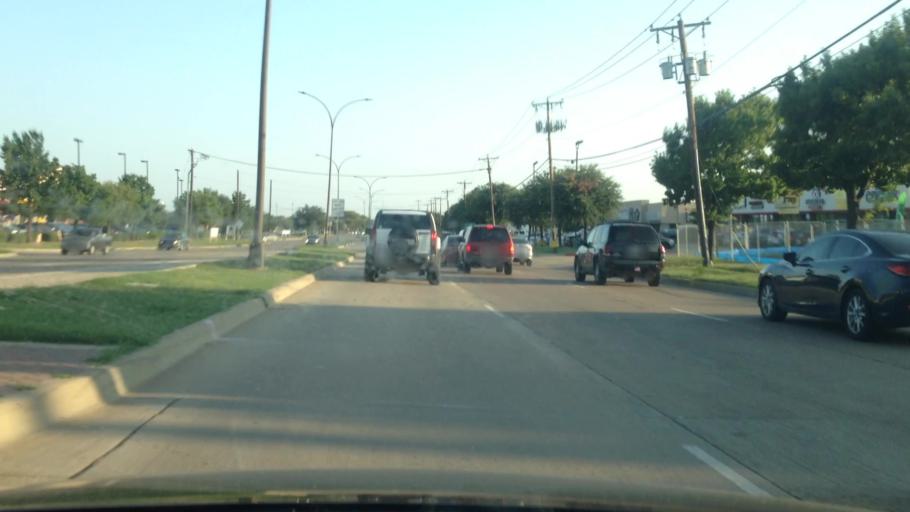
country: US
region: Texas
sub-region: Tarrant County
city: Dalworthington Gardens
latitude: 32.6739
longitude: -97.1150
